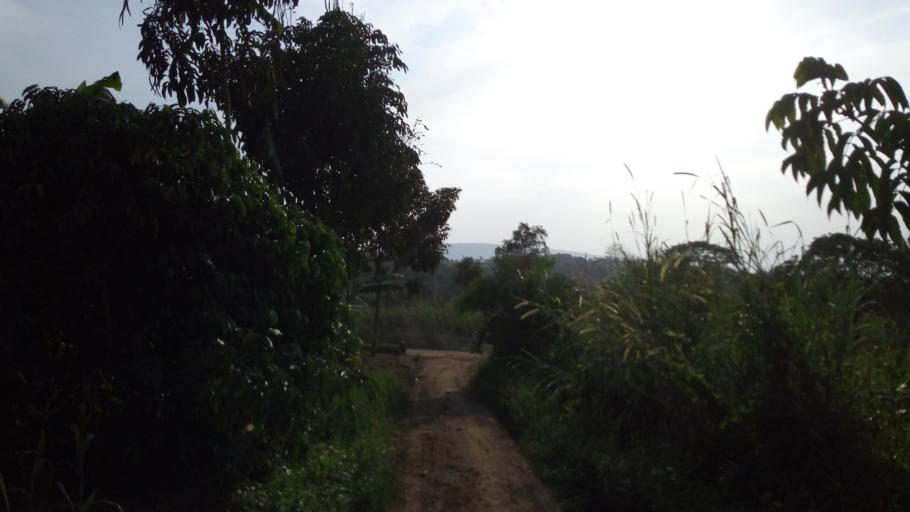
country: UG
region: Central Region
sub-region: Kiboga District
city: Kiboga
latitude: 0.7258
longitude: 31.7357
